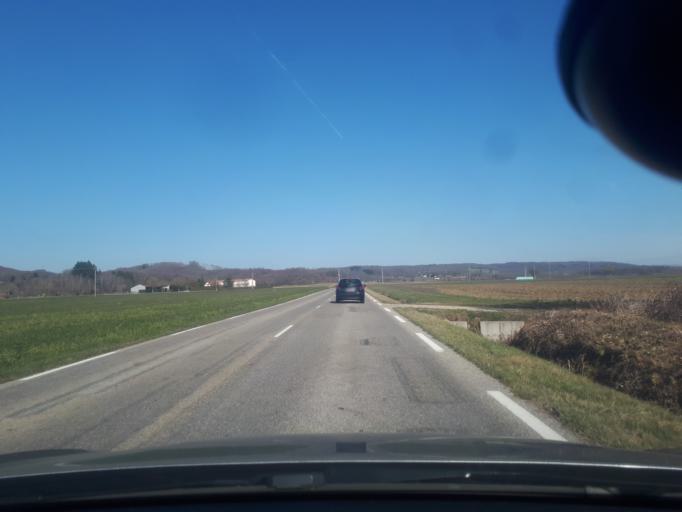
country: FR
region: Rhone-Alpes
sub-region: Departement de l'Isere
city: Champier
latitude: 45.4310
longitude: 5.2786
